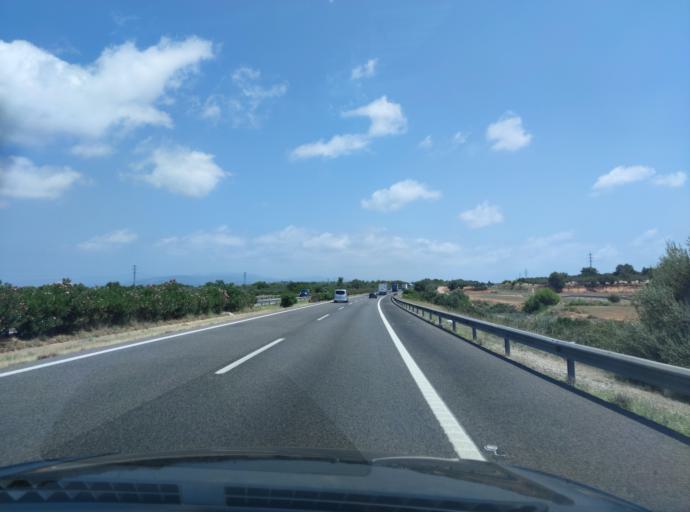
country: ES
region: Catalonia
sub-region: Provincia de Tarragona
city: Masdenverge
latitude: 40.6901
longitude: 0.5297
